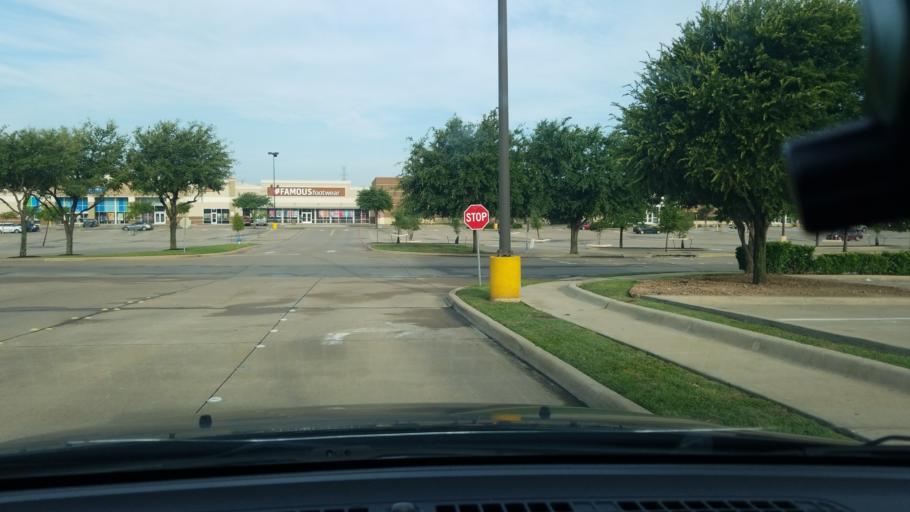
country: US
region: Texas
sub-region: Dallas County
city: Mesquite
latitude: 32.7970
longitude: -96.6270
